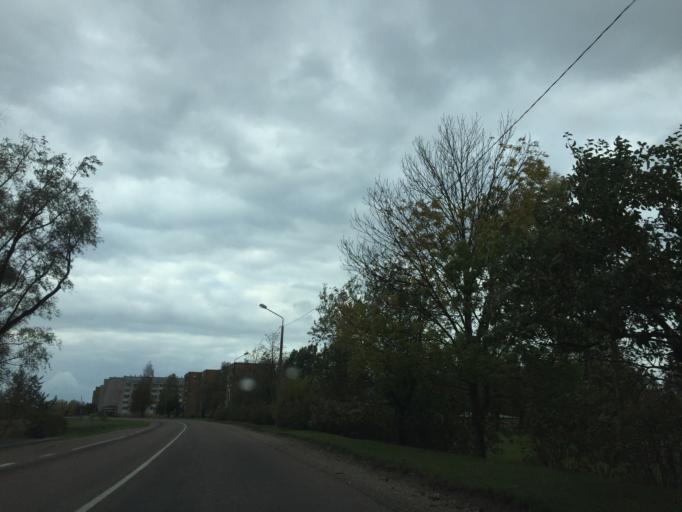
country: LV
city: Tireli
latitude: 56.7985
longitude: 23.6126
